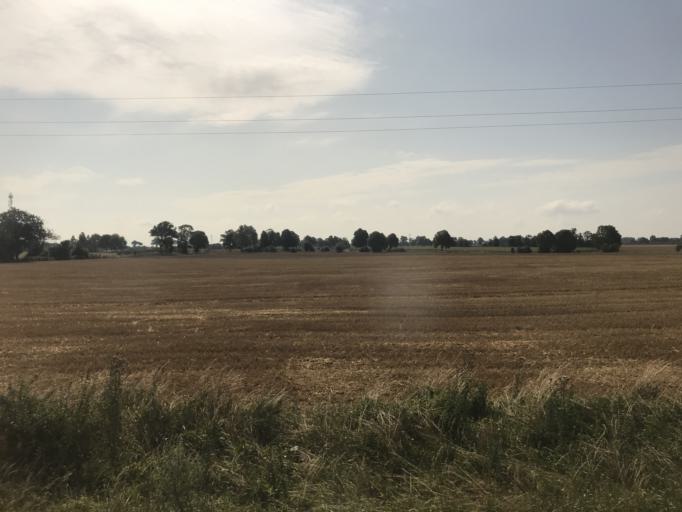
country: PL
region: Kujawsko-Pomorskie
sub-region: Powiat swiecki
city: Pruszcz
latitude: 53.3463
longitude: 18.2176
